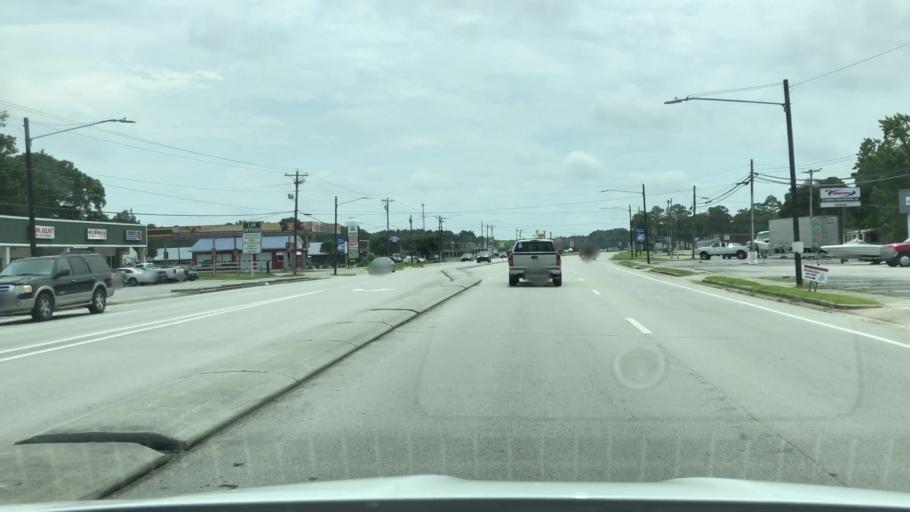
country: US
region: North Carolina
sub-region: Craven County
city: Havelock
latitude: 34.8669
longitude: -76.8996
